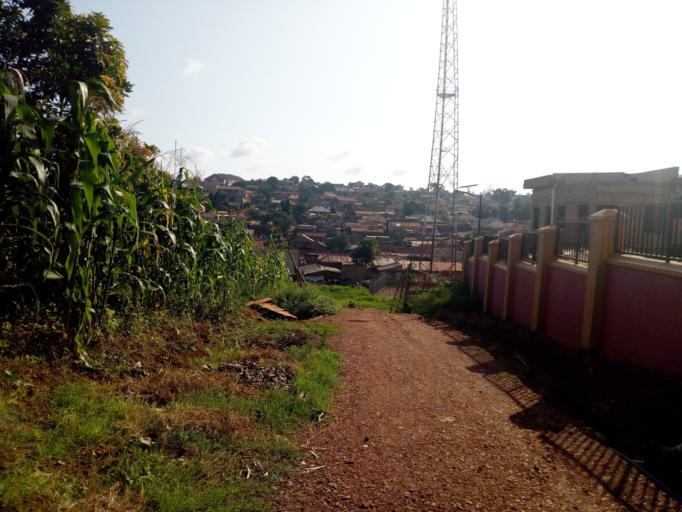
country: UG
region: Central Region
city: Kampala Central Division
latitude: 0.3388
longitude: 32.5596
